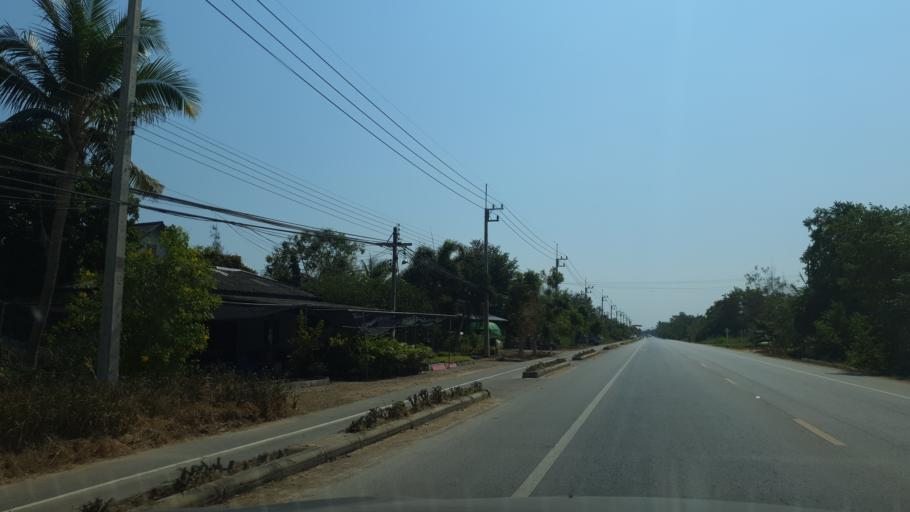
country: TH
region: Prachuap Khiri Khan
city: Pran Buri
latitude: 12.3551
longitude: 99.9381
